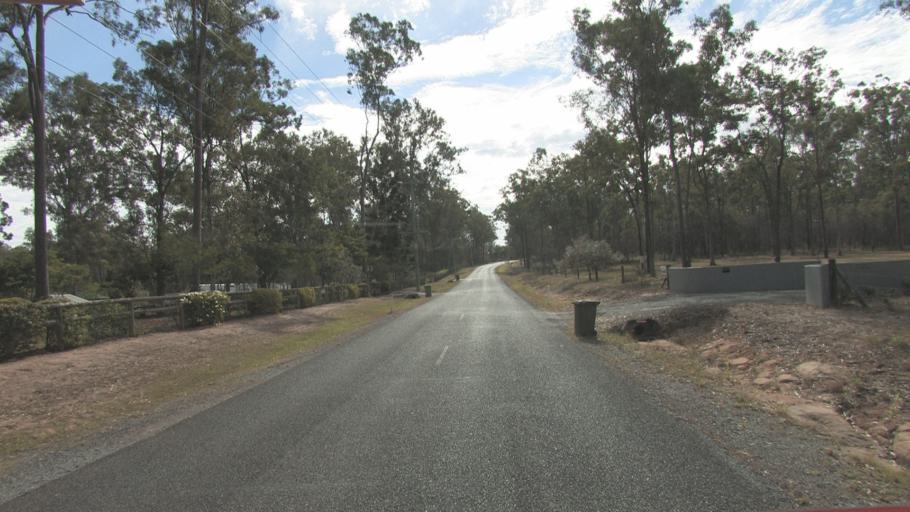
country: AU
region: Queensland
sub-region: Logan
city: North Maclean
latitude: -27.7452
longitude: 152.9735
